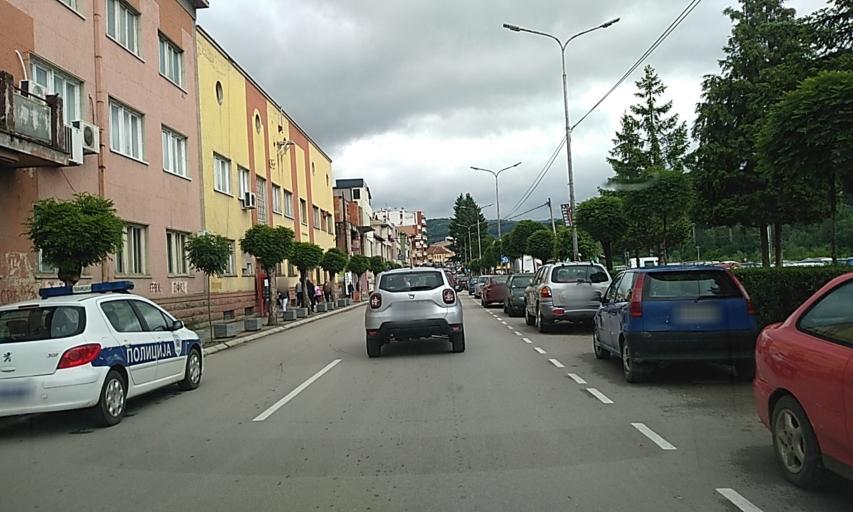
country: RS
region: Central Serbia
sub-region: Pcinjski Okrug
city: Vladicin Han
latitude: 42.7091
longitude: 22.0606
